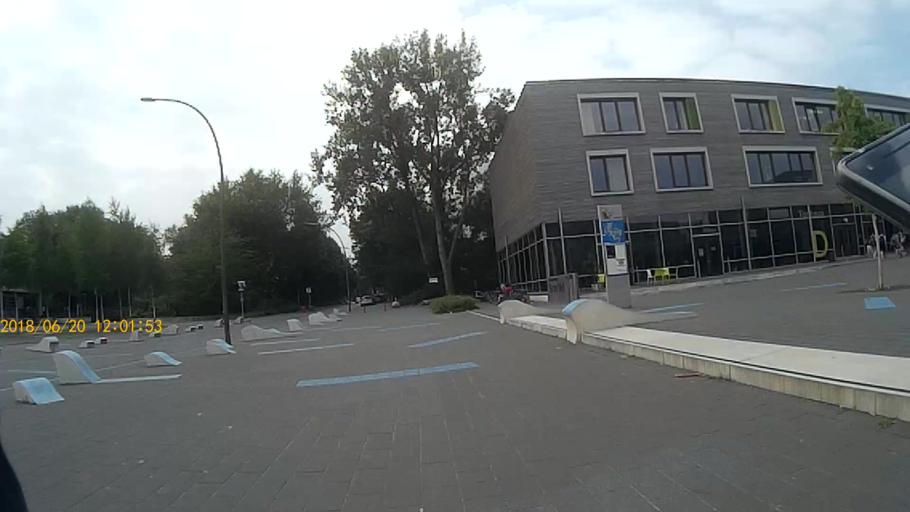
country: DE
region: Hamburg
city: Kleiner Grasbrook
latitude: 53.5001
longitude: 10.0129
